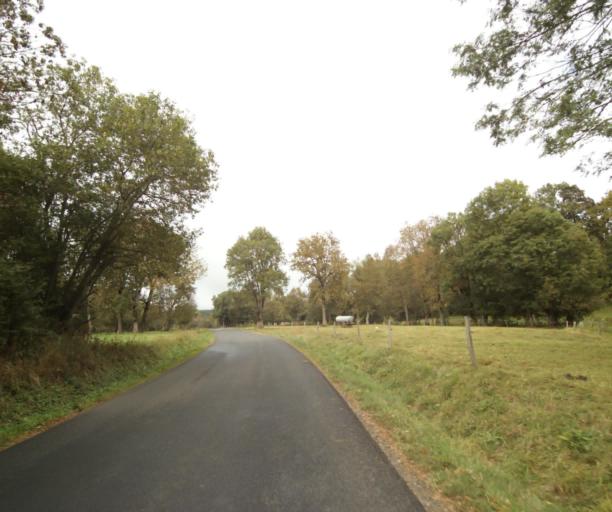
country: FR
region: Auvergne
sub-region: Departement du Puy-de-Dome
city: Saint-Genes-Champanelle
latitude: 45.7189
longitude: 2.9929
